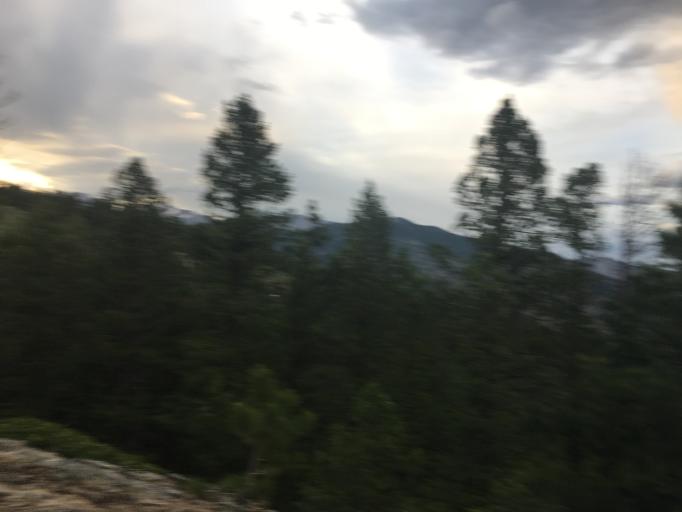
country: US
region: Colorado
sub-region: Larimer County
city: Estes Park
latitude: 40.3353
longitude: -105.5814
